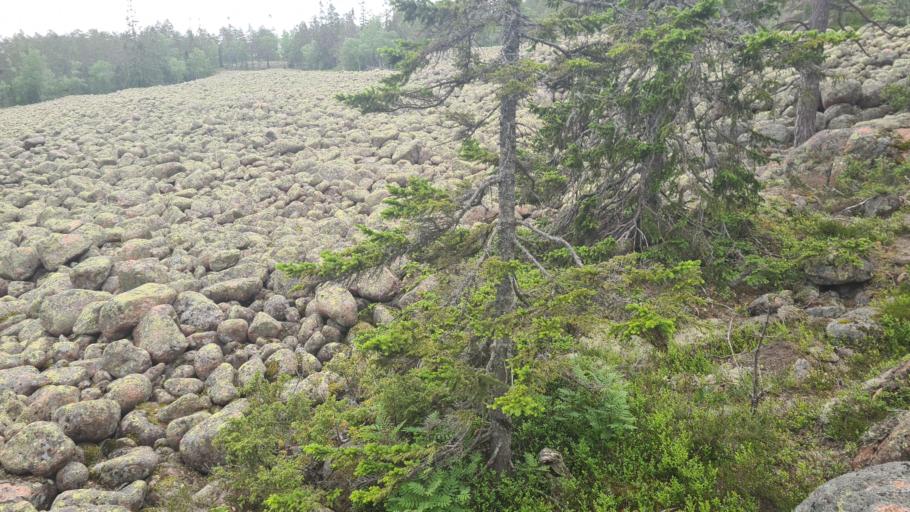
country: SE
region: Vaesternorrland
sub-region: Kramfors Kommun
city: Nordingra
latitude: 62.9835
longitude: 18.4011
